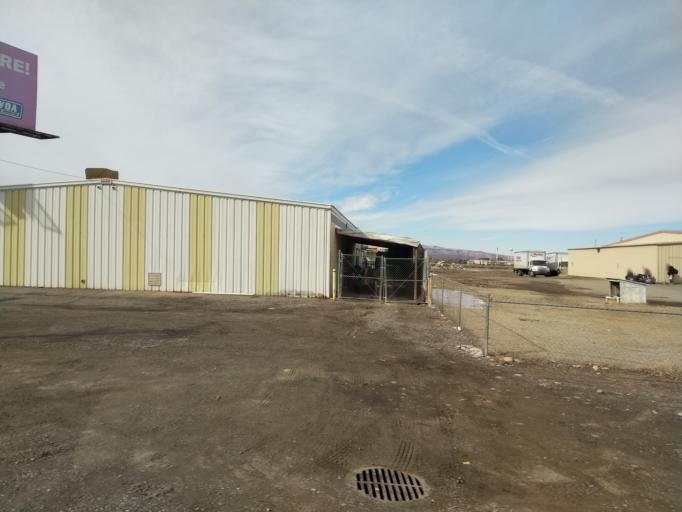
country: US
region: Colorado
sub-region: Mesa County
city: Grand Junction
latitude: 39.0726
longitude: -108.5244
